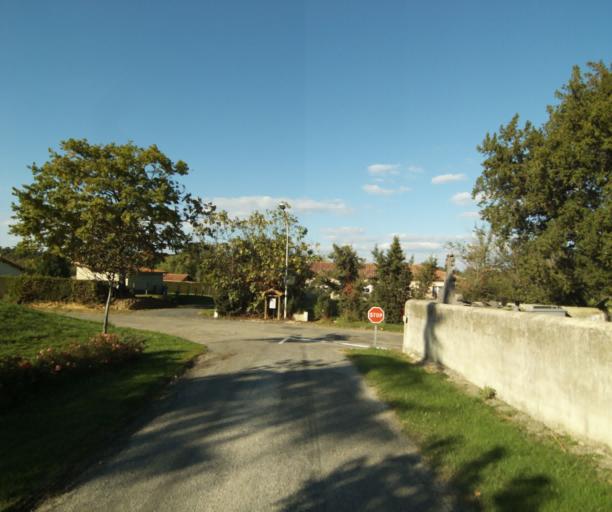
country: FR
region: Midi-Pyrenees
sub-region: Departement du Gers
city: Eauze
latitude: 43.7967
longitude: 0.1444
